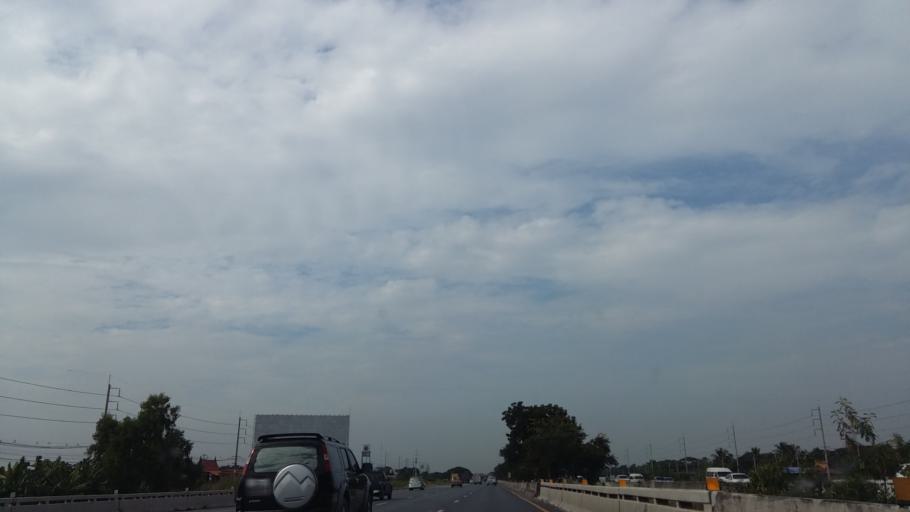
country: TH
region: Phra Nakhon Si Ayutthaya
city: Maha Rat
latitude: 14.4981
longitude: 100.5225
